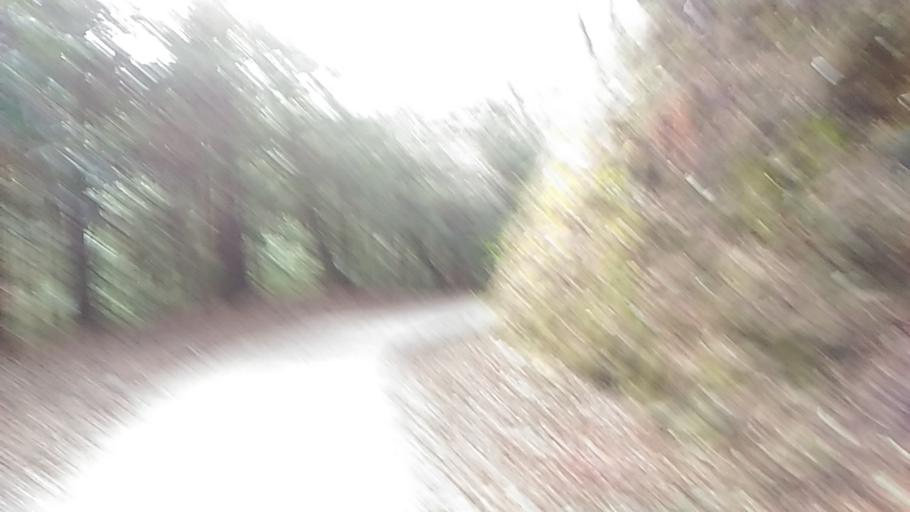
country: TW
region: Taiwan
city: Daxi
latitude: 24.4070
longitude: 121.3045
